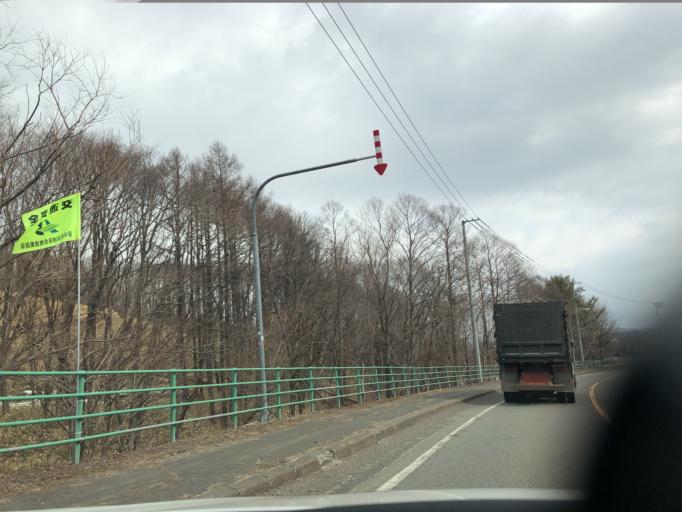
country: JP
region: Hokkaido
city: Chitose
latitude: 42.7635
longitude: 141.8044
